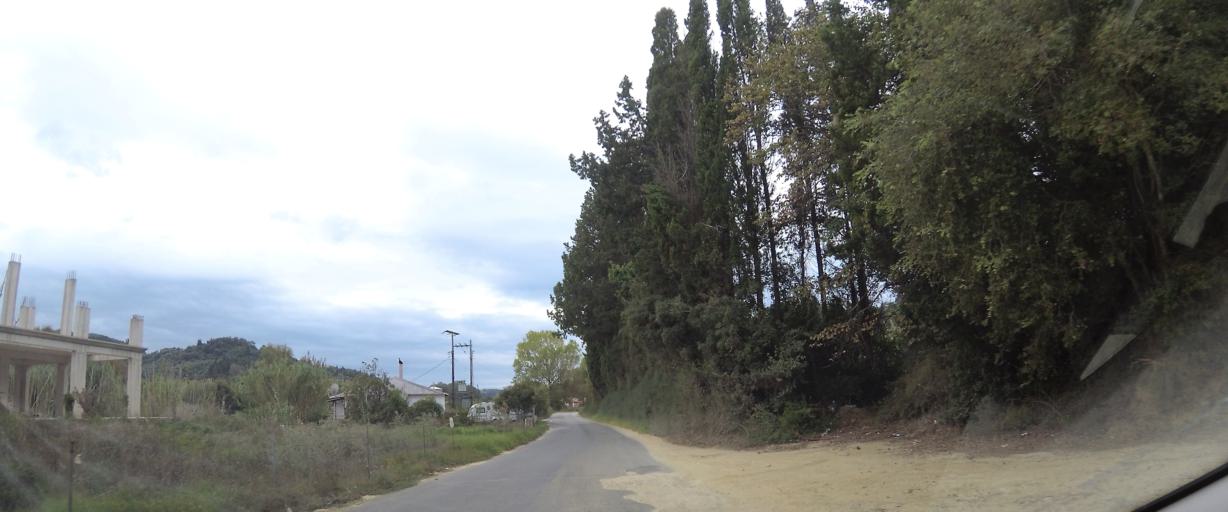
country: GR
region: Ionian Islands
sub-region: Nomos Kerkyras
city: Agios Georgis
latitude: 39.7671
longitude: 19.6973
